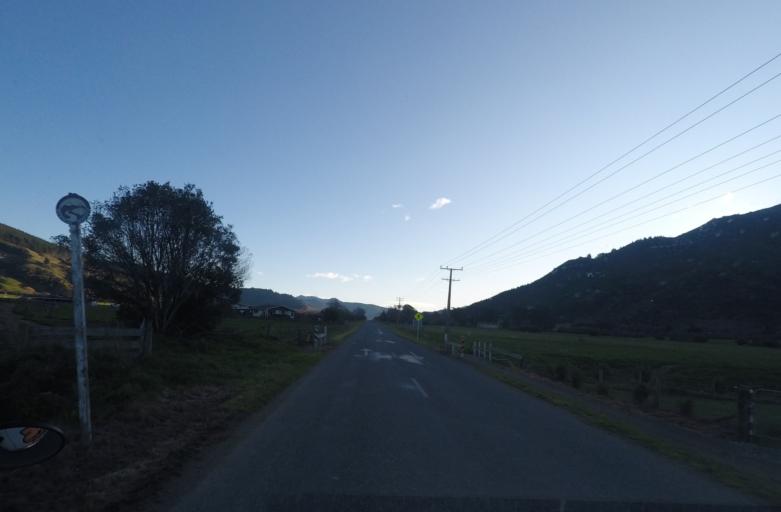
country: NZ
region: Marlborough
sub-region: Marlborough District
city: Picton
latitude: -41.2903
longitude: 173.8937
